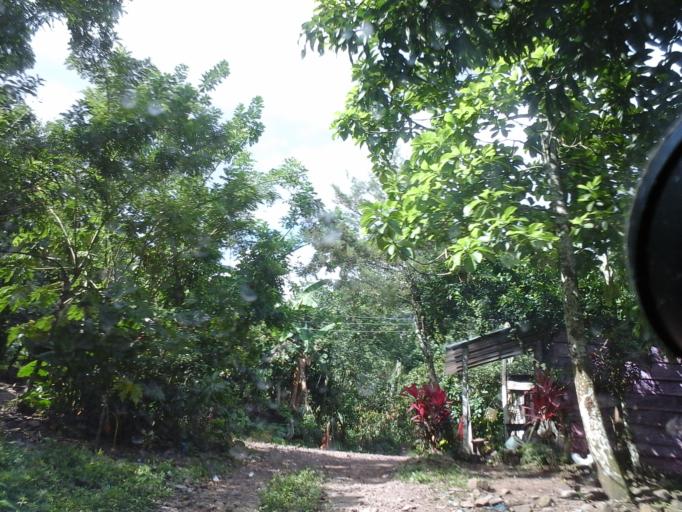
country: CO
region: Cesar
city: San Diego
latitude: 10.2847
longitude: -73.0875
